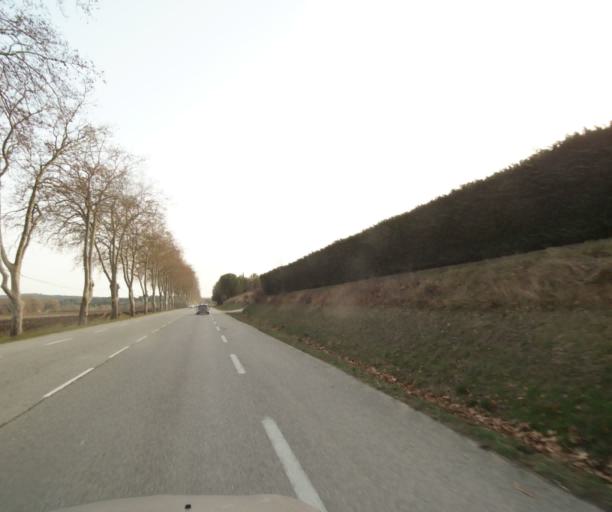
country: FR
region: Provence-Alpes-Cote d'Azur
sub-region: Departement des Bouches-du-Rhone
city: Rognes
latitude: 43.6509
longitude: 5.3576
